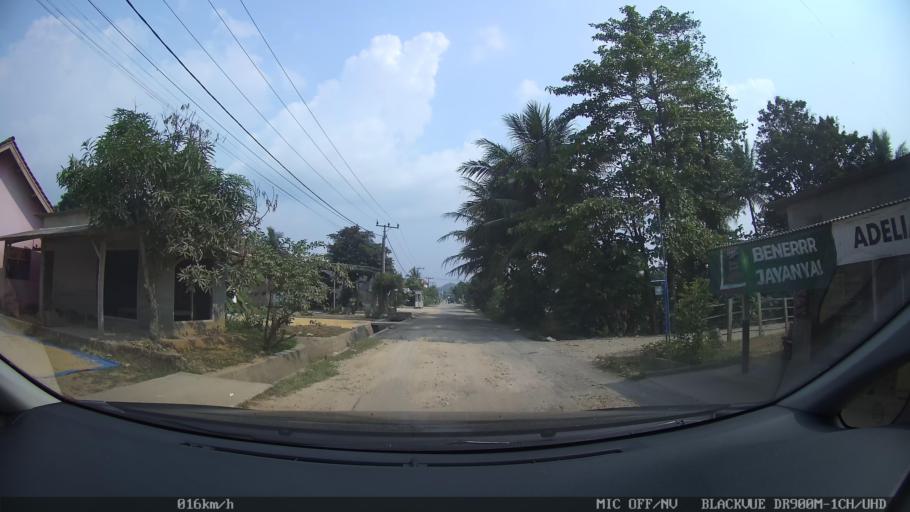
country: ID
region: Lampung
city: Pringsewu
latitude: -5.4082
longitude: 104.9927
